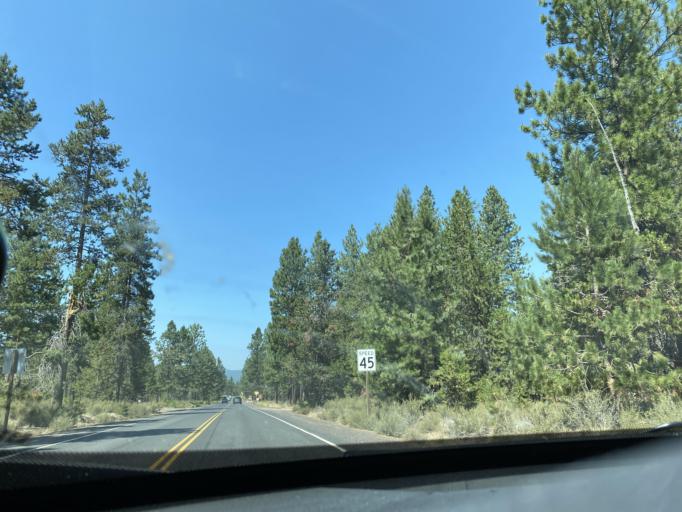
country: US
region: Oregon
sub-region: Deschutes County
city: Sunriver
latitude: 43.8924
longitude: -121.4098
